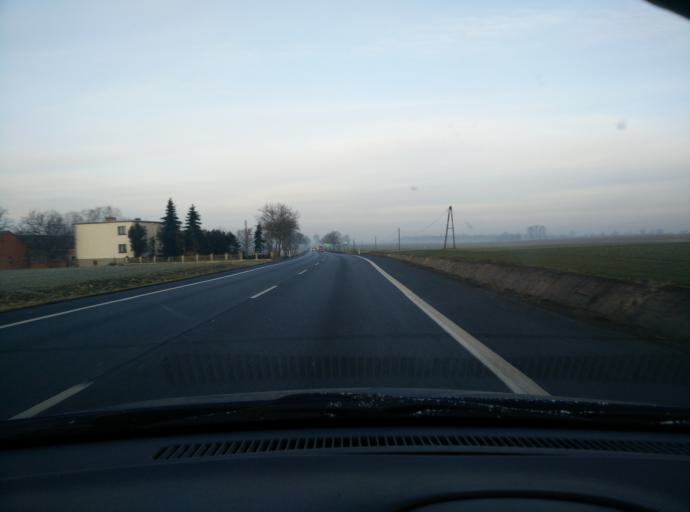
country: PL
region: Greater Poland Voivodeship
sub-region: Powiat poznanski
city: Kornik
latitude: 52.2418
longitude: 17.1415
